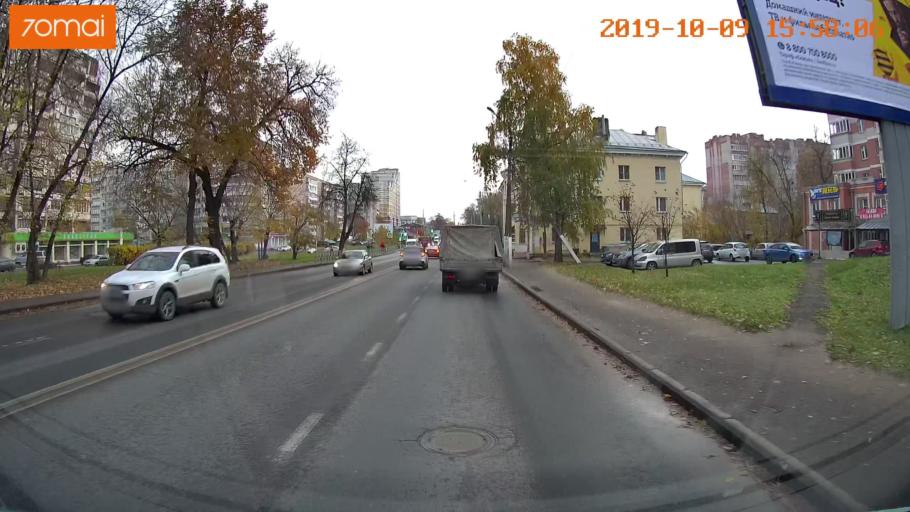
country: RU
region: Kostroma
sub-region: Kostromskoy Rayon
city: Kostroma
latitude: 57.7679
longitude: 40.9509
